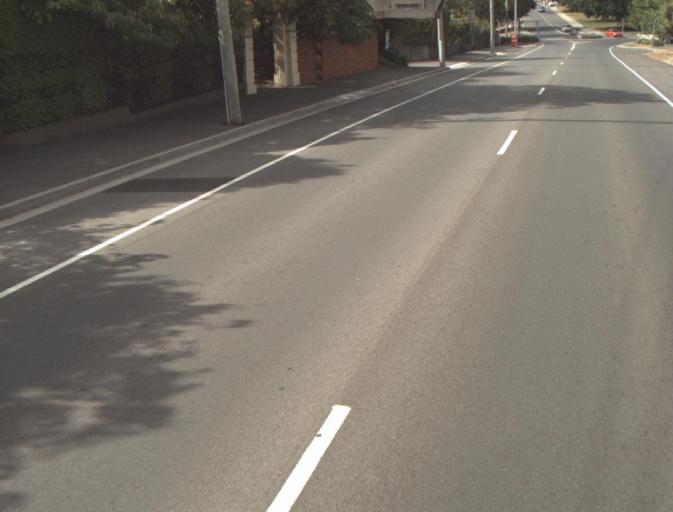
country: AU
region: Tasmania
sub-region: Launceston
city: East Launceston
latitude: -41.4373
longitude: 147.1472
